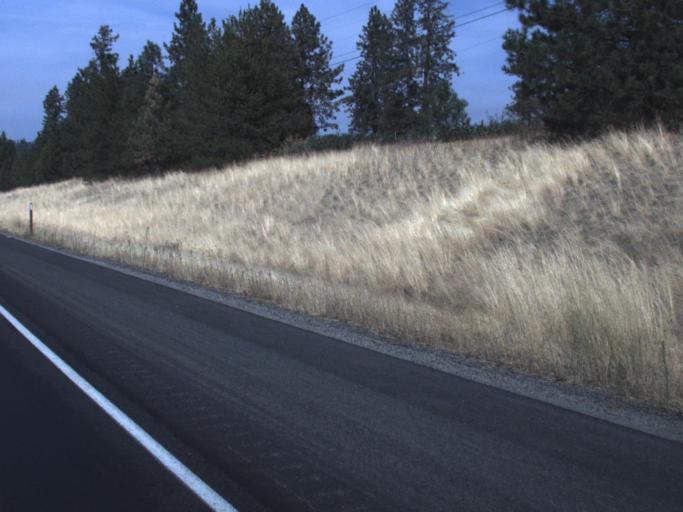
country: US
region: Washington
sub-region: Spokane County
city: Deer Park
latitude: 48.0566
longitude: -117.3441
